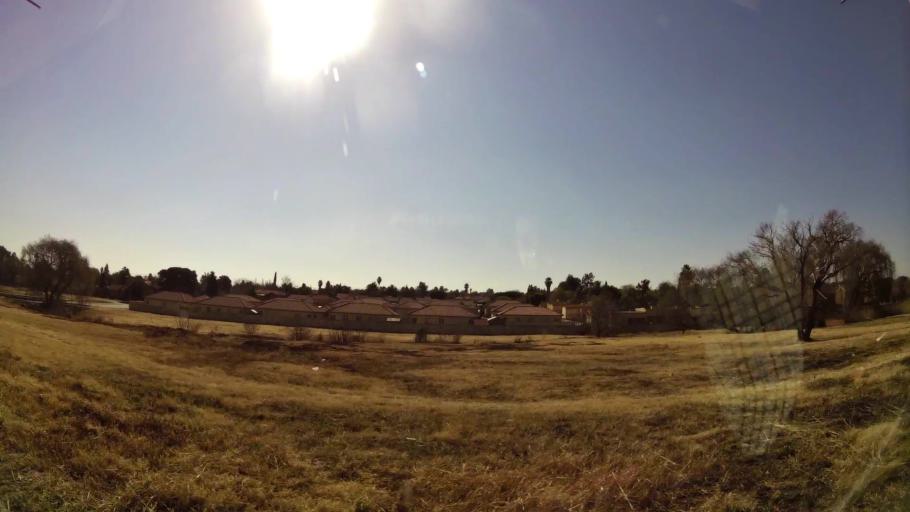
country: ZA
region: Gauteng
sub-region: Ekurhuleni Metropolitan Municipality
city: Tembisa
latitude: -26.0394
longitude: 28.2276
